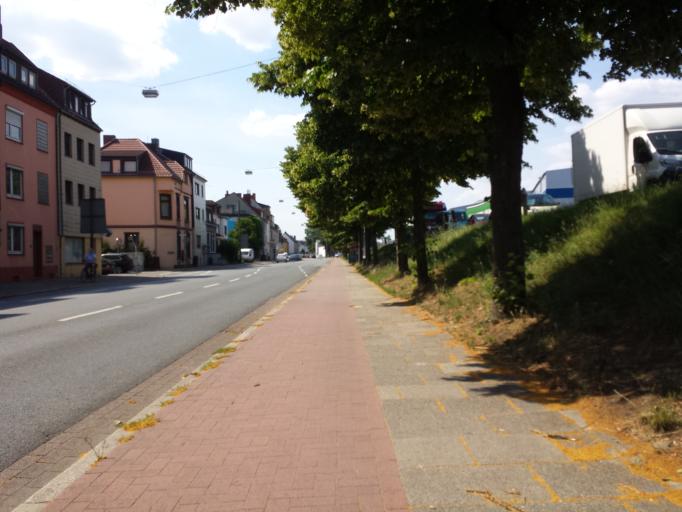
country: DE
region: Bremen
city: Bremen
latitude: 53.0781
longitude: 8.7810
